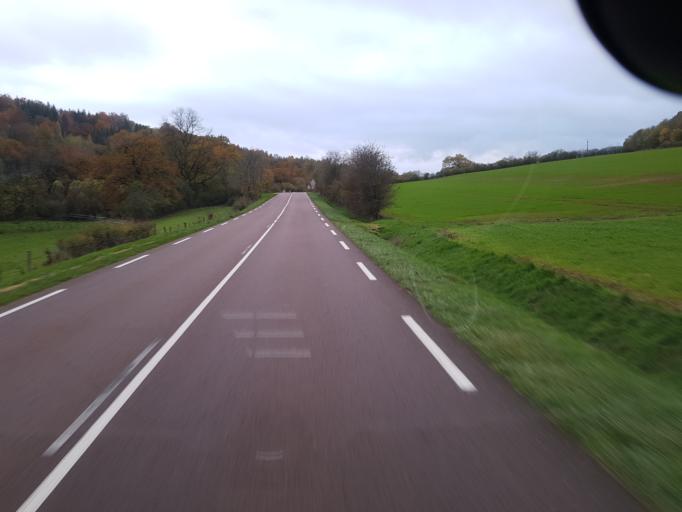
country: FR
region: Bourgogne
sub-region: Departement de la Cote-d'Or
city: Chatillon-sur-Seine
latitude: 47.6768
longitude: 4.6955
